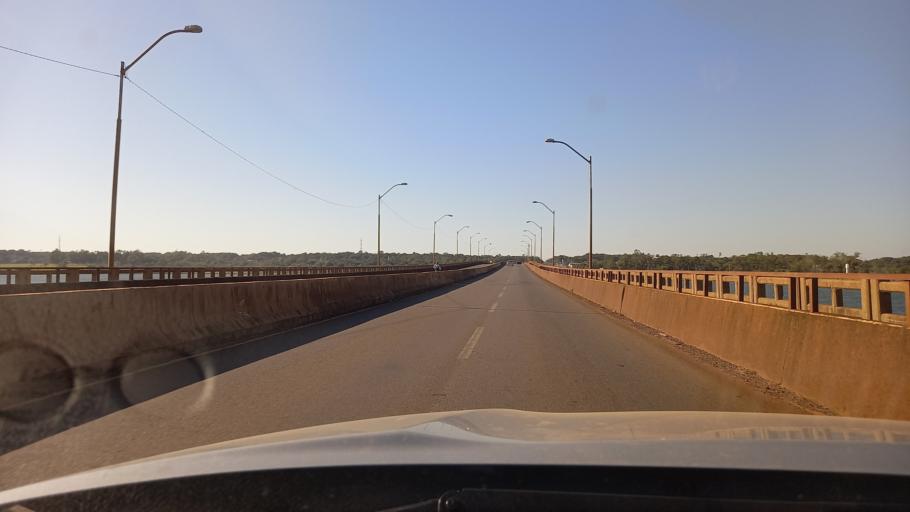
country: PY
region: Itapua
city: Encarnacion
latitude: -27.2984
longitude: -55.9045
